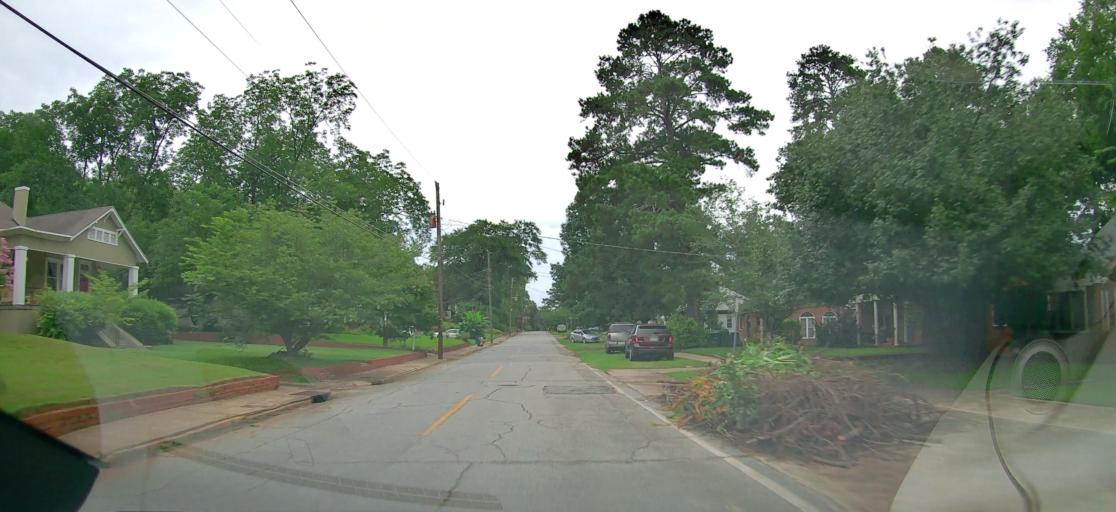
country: US
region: Georgia
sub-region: Bibb County
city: Macon
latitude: 32.8539
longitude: -83.6262
